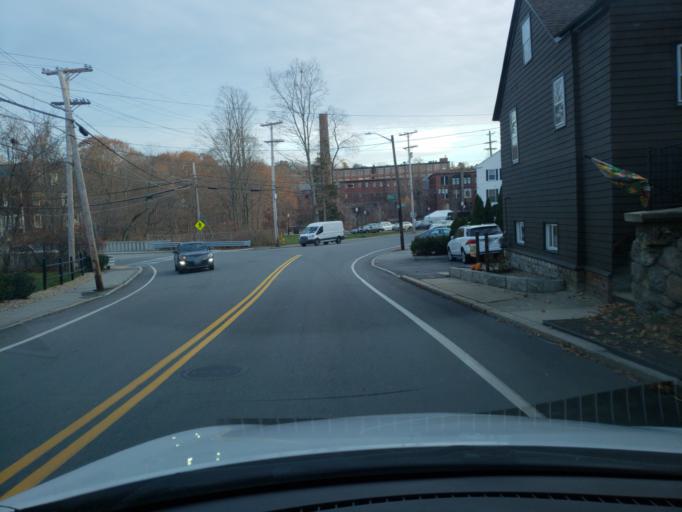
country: US
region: Massachusetts
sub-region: Essex County
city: Andover
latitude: 42.6575
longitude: -71.1475
